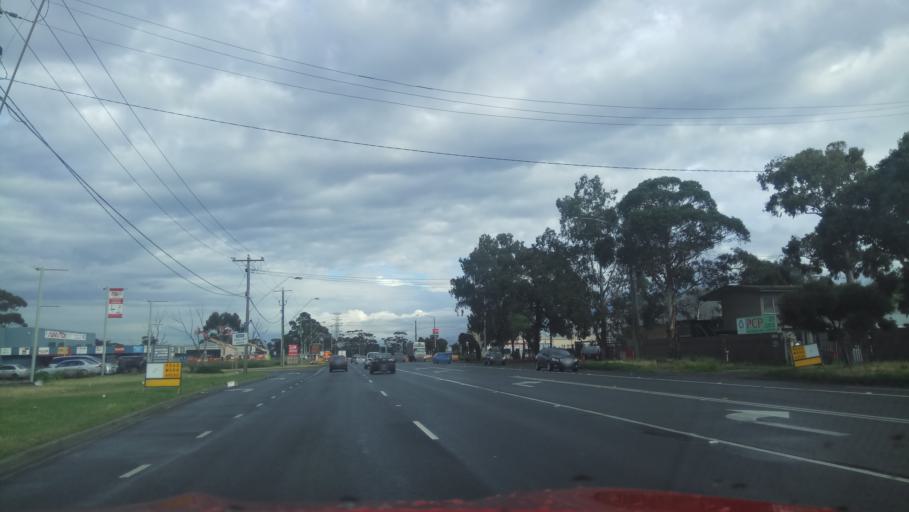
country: AU
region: Victoria
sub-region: Brimbank
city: Brooklyn
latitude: -37.8205
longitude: 144.8209
